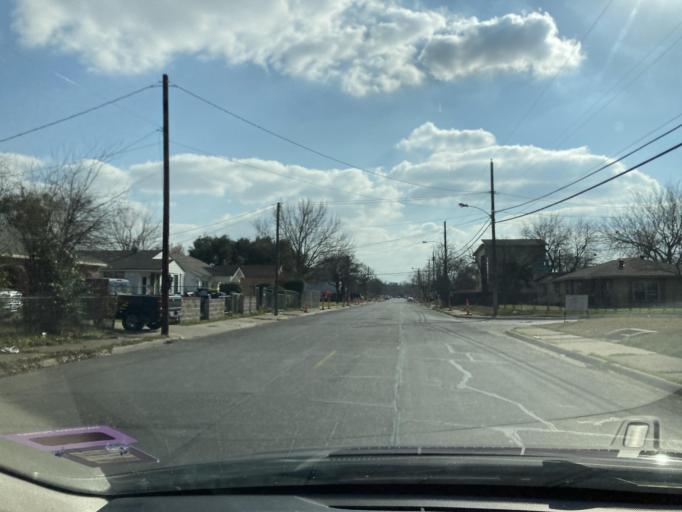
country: US
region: Texas
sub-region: Dallas County
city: Dallas
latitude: 32.7898
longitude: -96.8479
